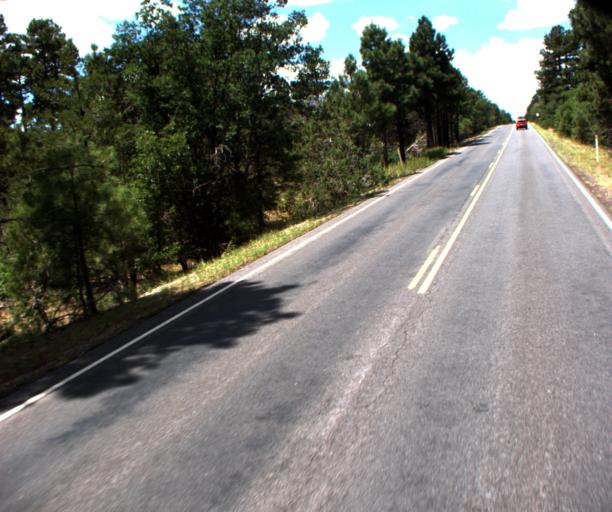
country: US
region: Arizona
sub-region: Coconino County
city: Grand Canyon
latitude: 36.0027
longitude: -112.0421
